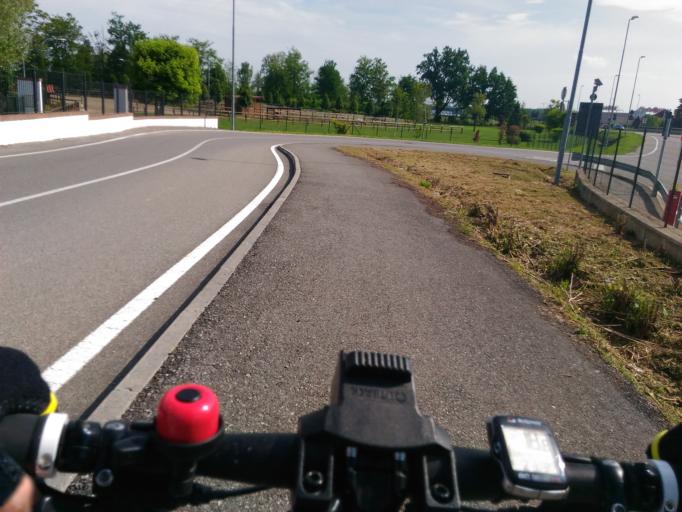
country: IT
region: Lombardy
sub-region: Provincia di Lodi
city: Muzza di Cornegliano Laudense
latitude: 45.2850
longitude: 9.4667
